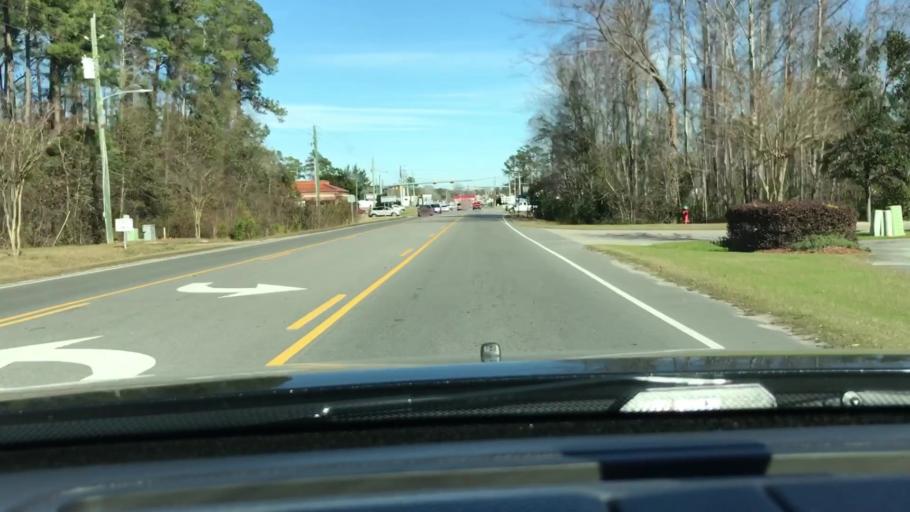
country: US
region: North Carolina
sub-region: Brunswick County
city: Shallotte
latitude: 33.9675
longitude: -78.3926
